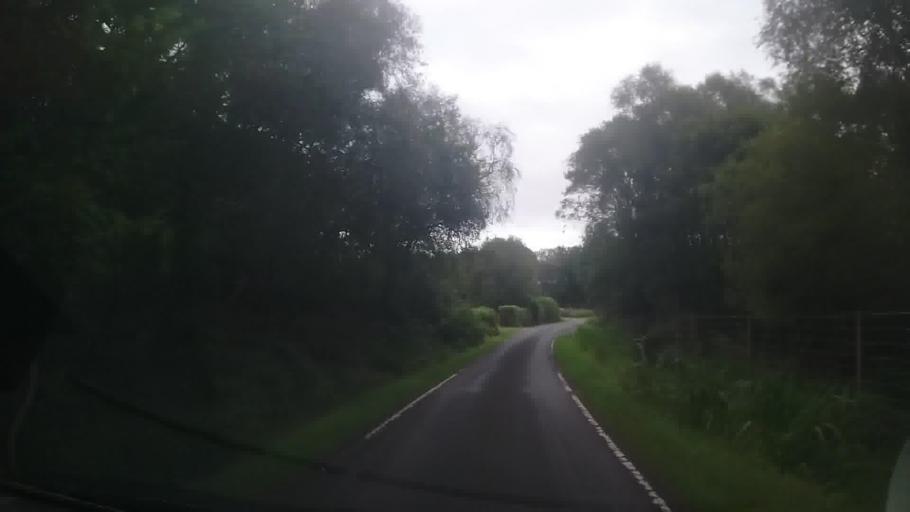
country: GB
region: Scotland
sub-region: Argyll and Bute
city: Isle Of Mull
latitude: 56.7080
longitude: -5.7817
